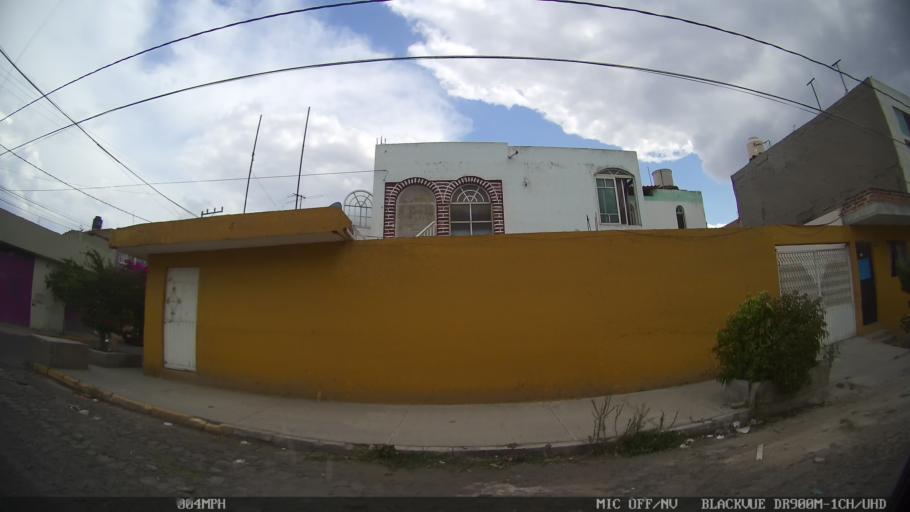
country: MX
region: Jalisco
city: Tlaquepaque
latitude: 20.6307
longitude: -103.2744
